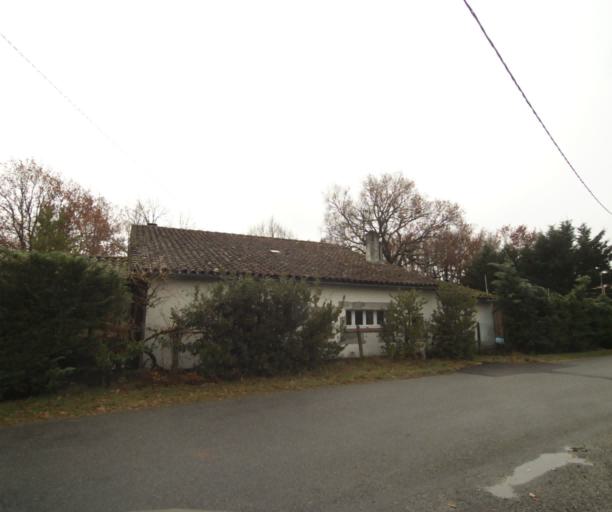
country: FR
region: Midi-Pyrenees
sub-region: Departement de la Haute-Garonne
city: Villemur-sur-Tarn
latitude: 43.8580
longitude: 1.4740
